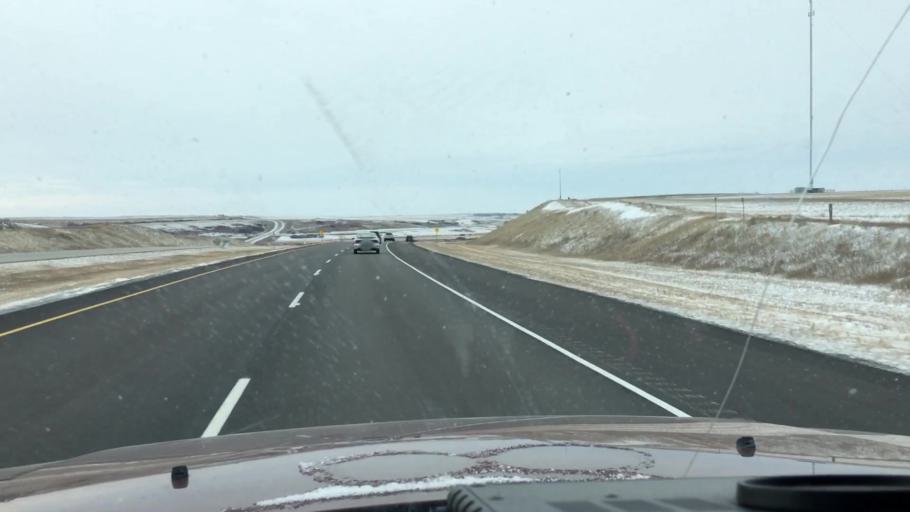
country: CA
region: Saskatchewan
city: Saskatoon
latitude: 51.7391
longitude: -106.4765
